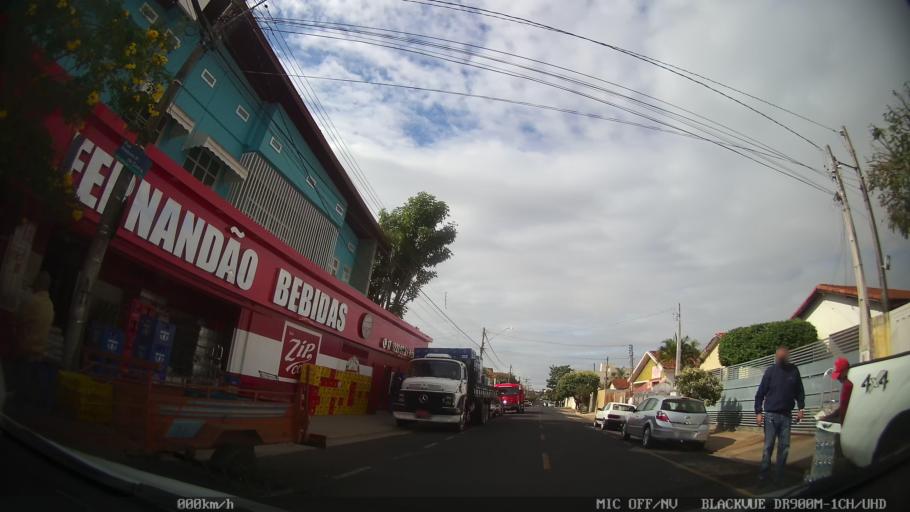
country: BR
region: Sao Paulo
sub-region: Sao Jose Do Rio Preto
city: Sao Jose do Rio Preto
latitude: -20.8355
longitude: -49.3747
